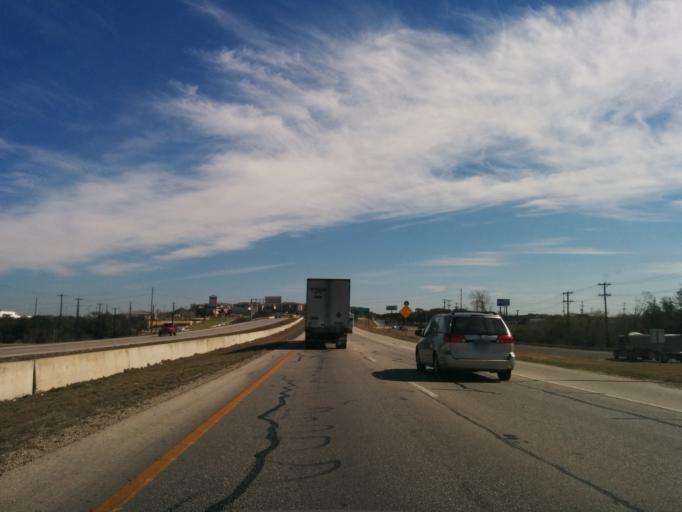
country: US
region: Texas
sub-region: Bexar County
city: Shavano Park
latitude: 29.5981
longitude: -98.5669
